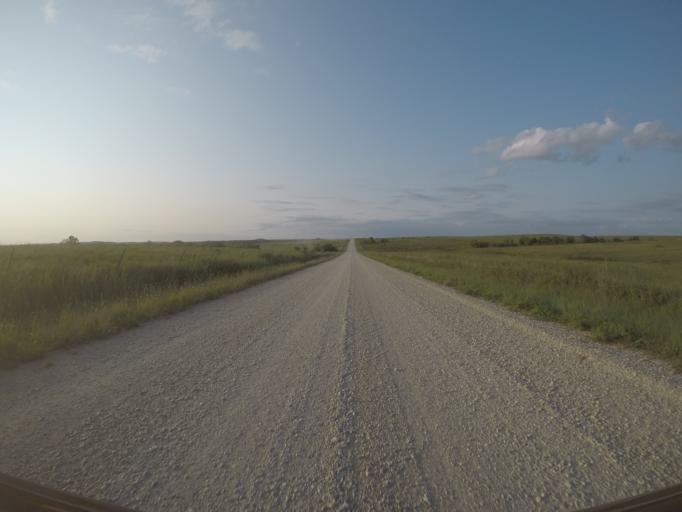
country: US
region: Kansas
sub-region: Pottawatomie County
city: Wamego
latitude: 39.1201
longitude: -96.4282
